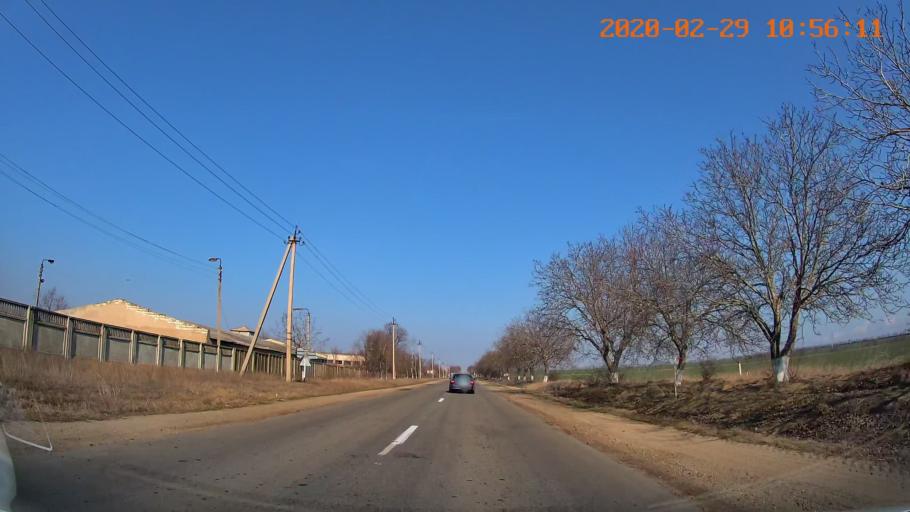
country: MD
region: Telenesti
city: Grigoriopol
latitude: 47.1428
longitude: 29.3253
